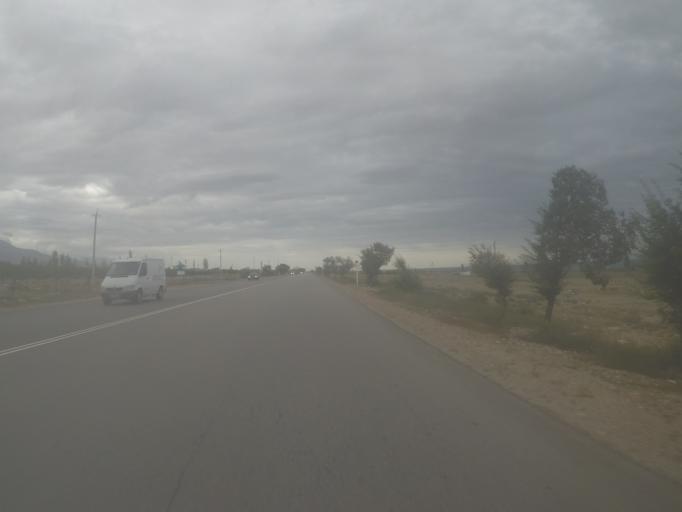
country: KG
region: Ysyk-Koel
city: Cholpon-Ata
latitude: 42.5972
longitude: 76.8230
